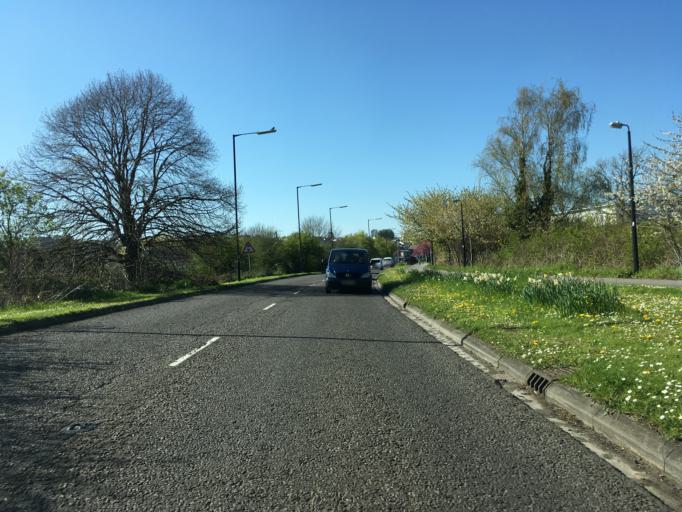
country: GB
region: England
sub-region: North Somerset
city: Portishead
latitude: 51.4820
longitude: -2.7633
